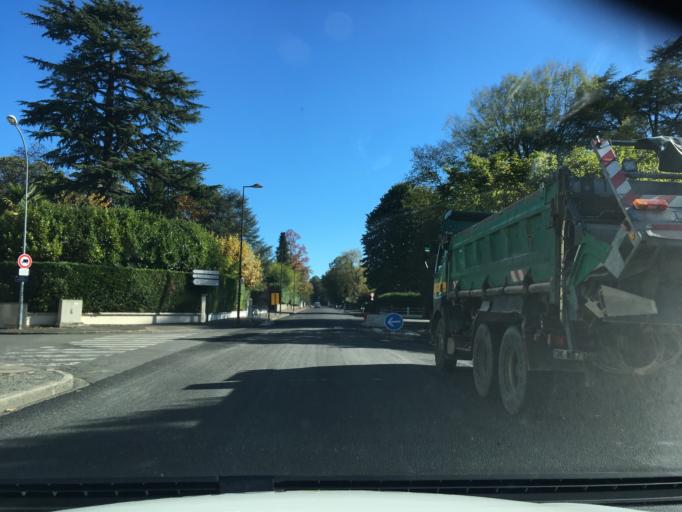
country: FR
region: Aquitaine
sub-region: Departement des Pyrenees-Atlantiques
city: Bizanos
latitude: 43.2989
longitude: -0.3455
